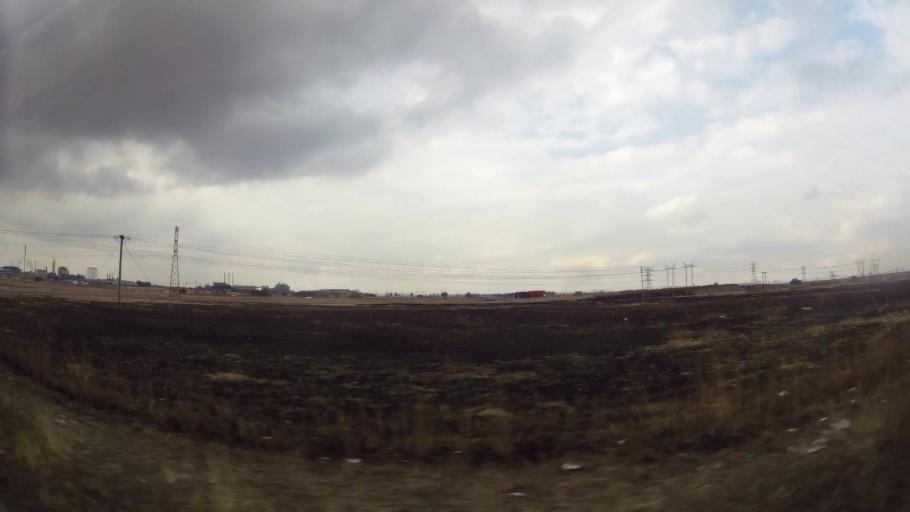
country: ZA
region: Orange Free State
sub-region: Fezile Dabi District Municipality
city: Sasolburg
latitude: -26.8394
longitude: 27.8714
